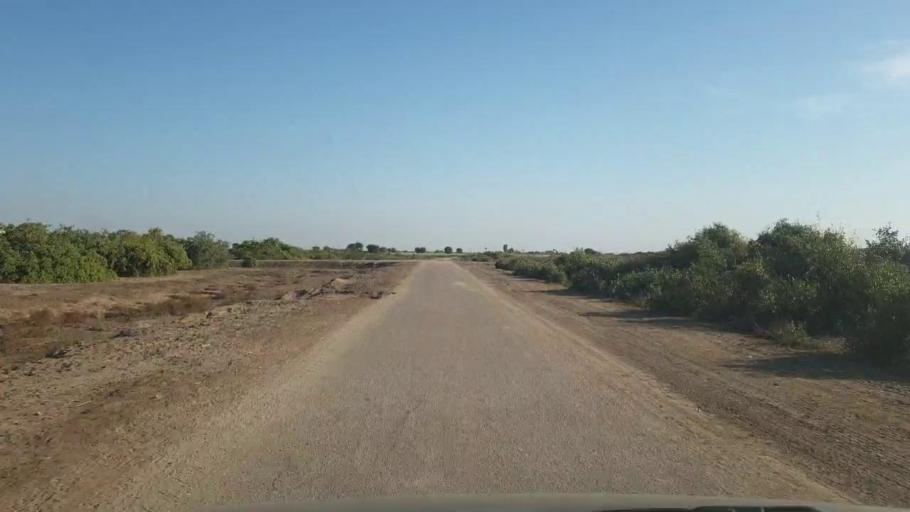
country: PK
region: Sindh
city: Dhoro Naro
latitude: 25.4262
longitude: 69.5337
